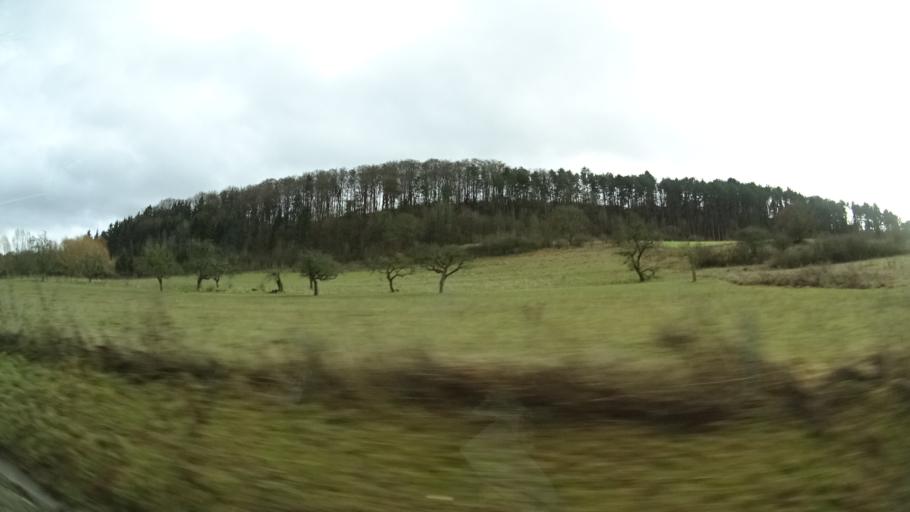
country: DE
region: Thuringia
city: Oberkatz
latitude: 50.6056
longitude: 10.2306
